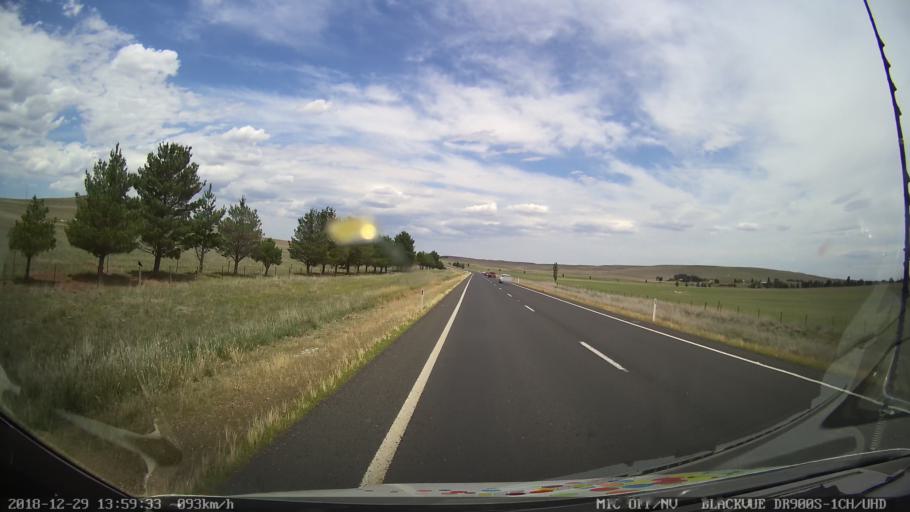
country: AU
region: New South Wales
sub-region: Cooma-Monaro
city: Cooma
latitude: -36.2541
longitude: 149.1498
